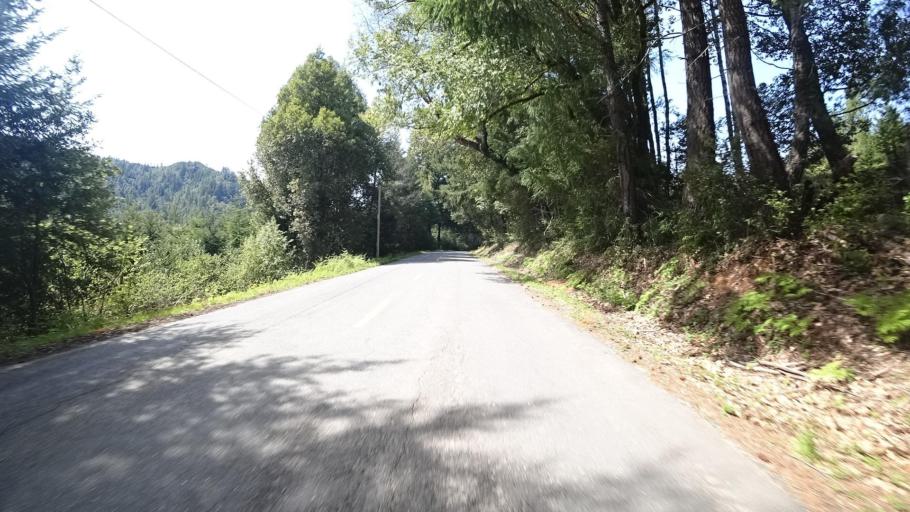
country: US
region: California
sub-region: Humboldt County
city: Redway
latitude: 40.3710
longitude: -123.7364
